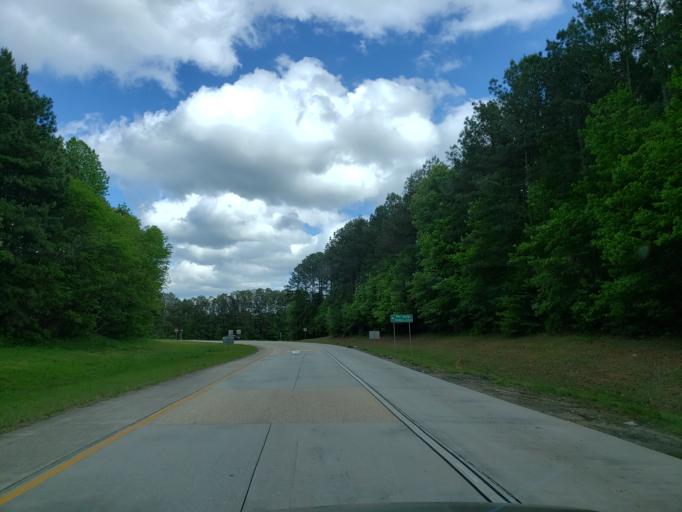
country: US
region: Georgia
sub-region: Carroll County
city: Mount Zion
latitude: 33.6883
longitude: -85.1898
